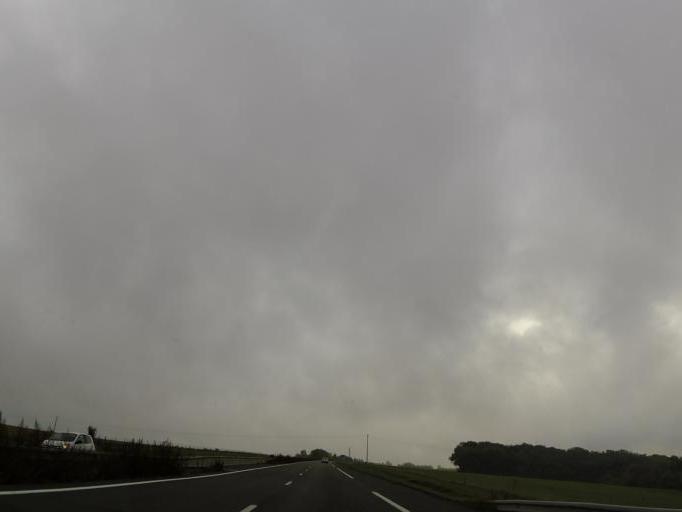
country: FR
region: Ile-de-France
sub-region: Departement de Seine-et-Marne
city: Bouleurs
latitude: 48.9038
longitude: 2.9337
